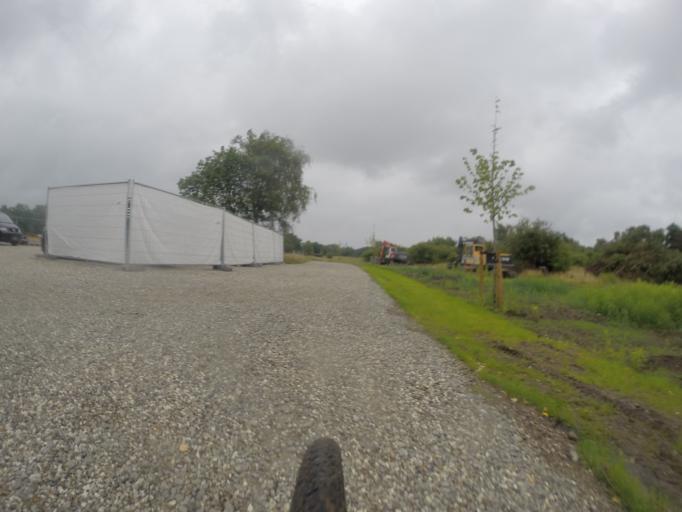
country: DK
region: Capital Region
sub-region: Herlev Kommune
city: Herlev
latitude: 55.7522
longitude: 12.4379
